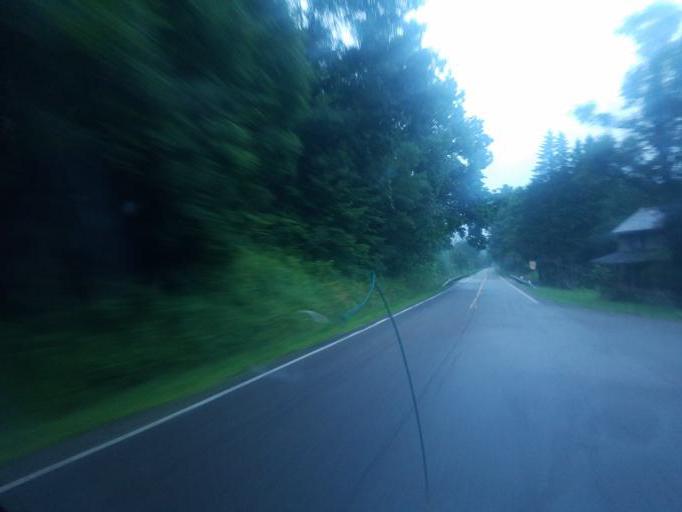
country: US
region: Ohio
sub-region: Carroll County
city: Carrollton
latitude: 40.5731
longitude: -81.0457
